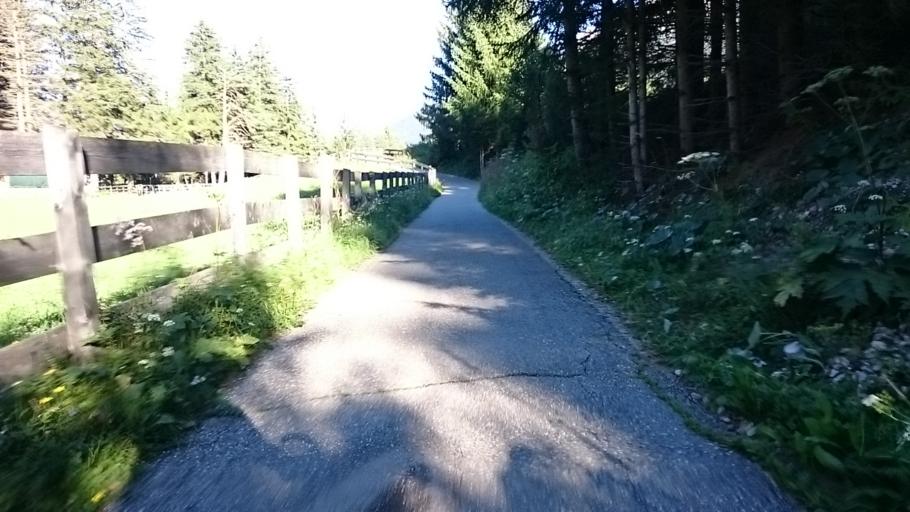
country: IT
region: Trentino-Alto Adige
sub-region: Bolzano
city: Dobbiaco
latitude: 46.7284
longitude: 12.2106
